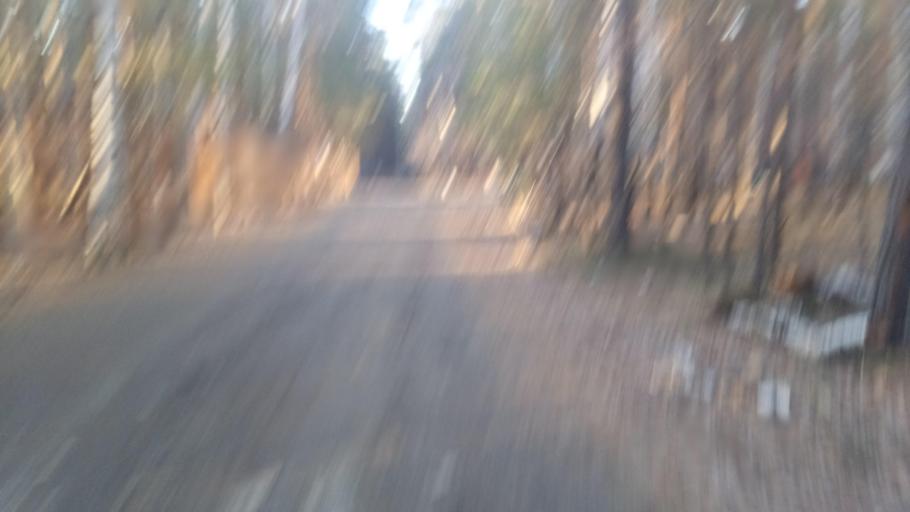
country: RU
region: Chelyabinsk
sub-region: Gorod Chelyabinsk
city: Chelyabinsk
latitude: 55.1280
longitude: 61.3485
